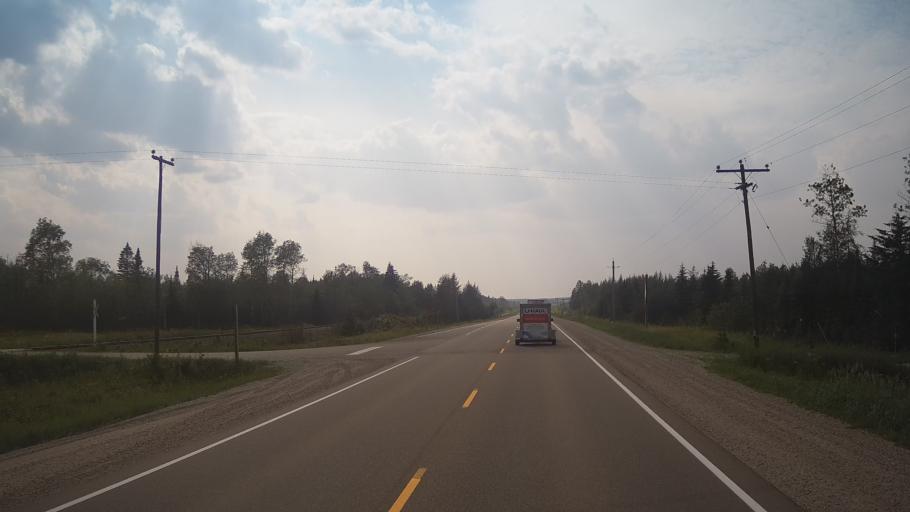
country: CA
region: Ontario
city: Kapuskasing
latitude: 49.5217
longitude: -82.8253
